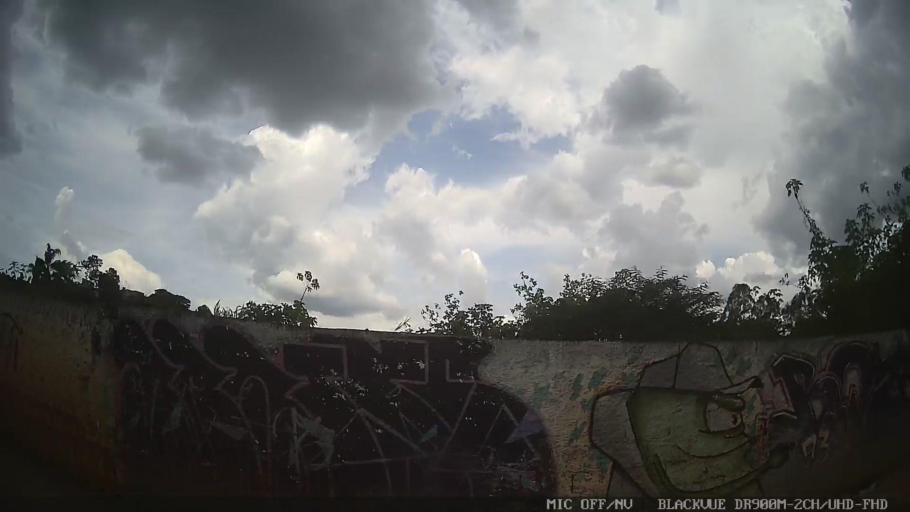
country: BR
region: Sao Paulo
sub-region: Ferraz De Vasconcelos
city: Ferraz de Vasconcelos
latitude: -23.5574
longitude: -46.3586
